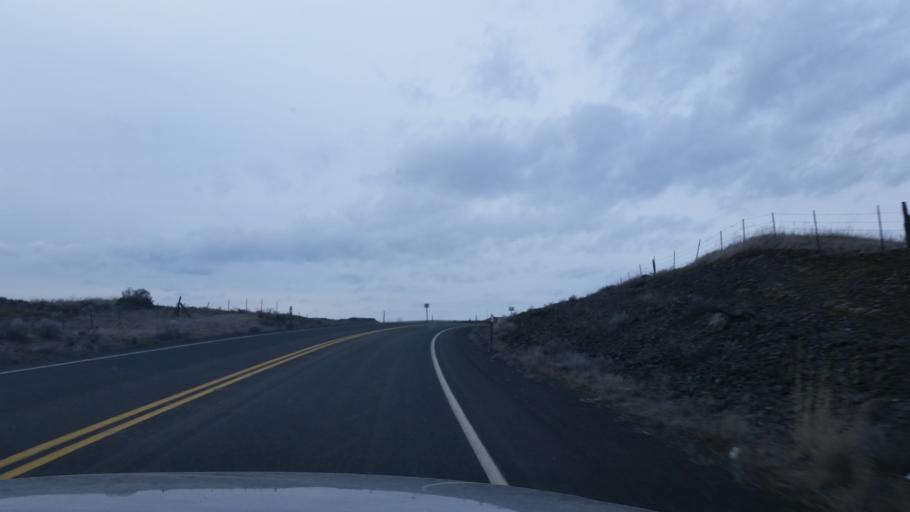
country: US
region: Washington
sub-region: Spokane County
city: Medical Lake
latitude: 47.2747
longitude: -117.9544
